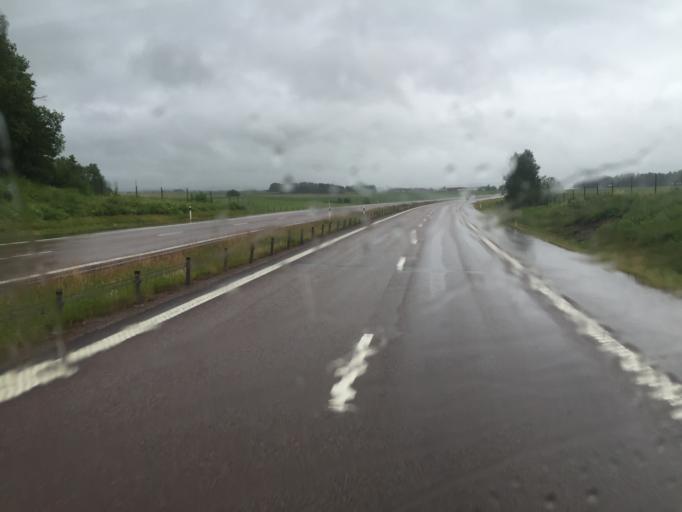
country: SE
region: Dalarna
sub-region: Borlange Kommun
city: Ornas
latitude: 60.4935
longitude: 15.5019
